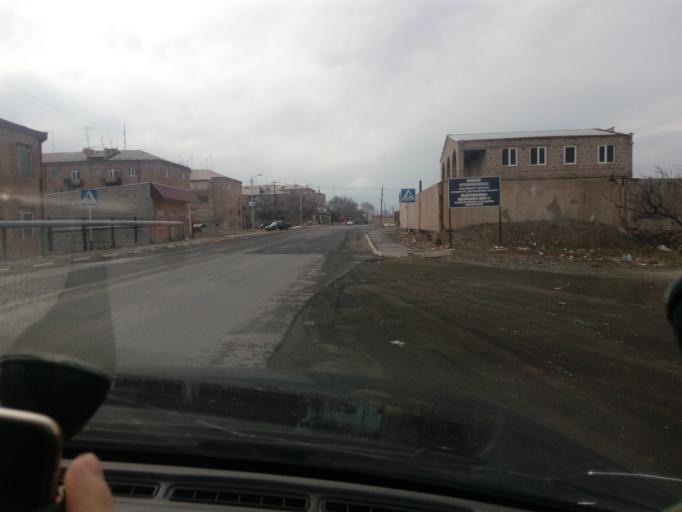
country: AM
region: Aragatsotn
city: Arteni
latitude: 40.3173
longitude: 43.6825
